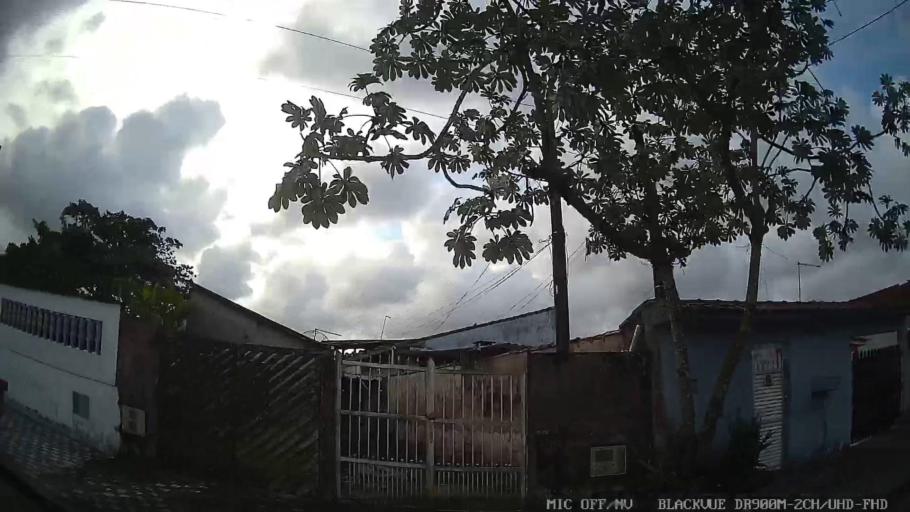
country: BR
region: Sao Paulo
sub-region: Mongagua
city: Mongagua
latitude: -24.1192
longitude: -46.6758
